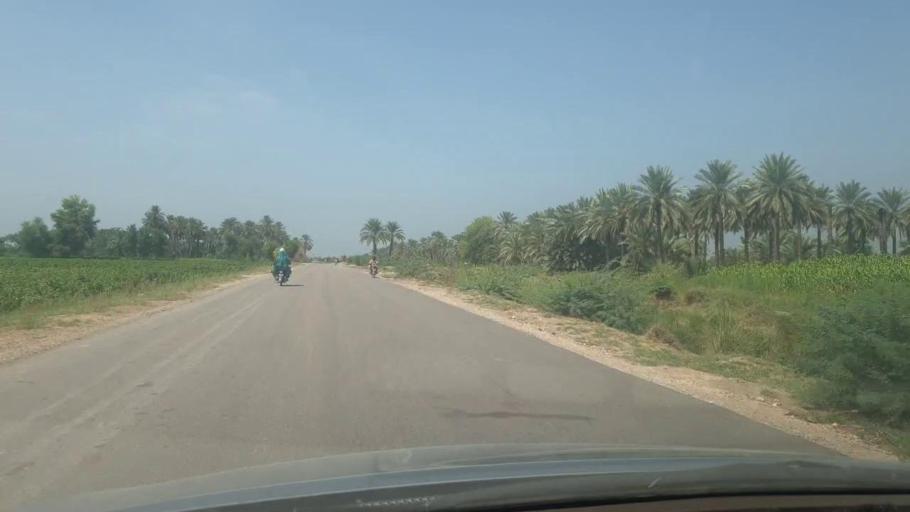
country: PK
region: Sindh
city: Ranipur
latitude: 27.2439
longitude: 68.5766
